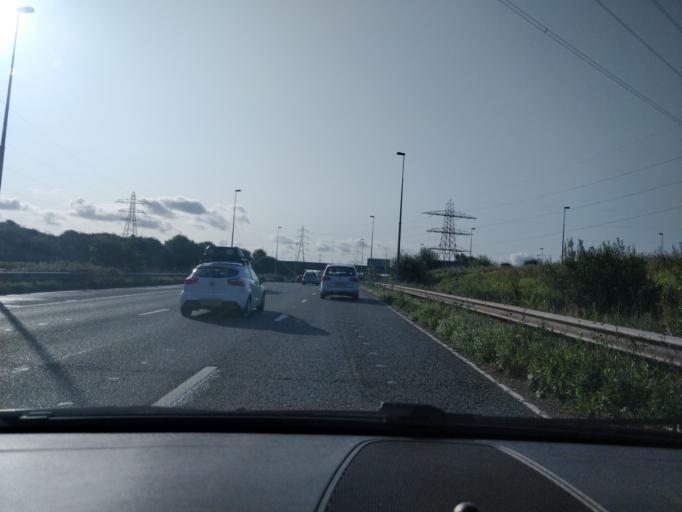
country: GB
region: England
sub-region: Sefton
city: Maghull
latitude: 53.4927
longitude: -2.9495
